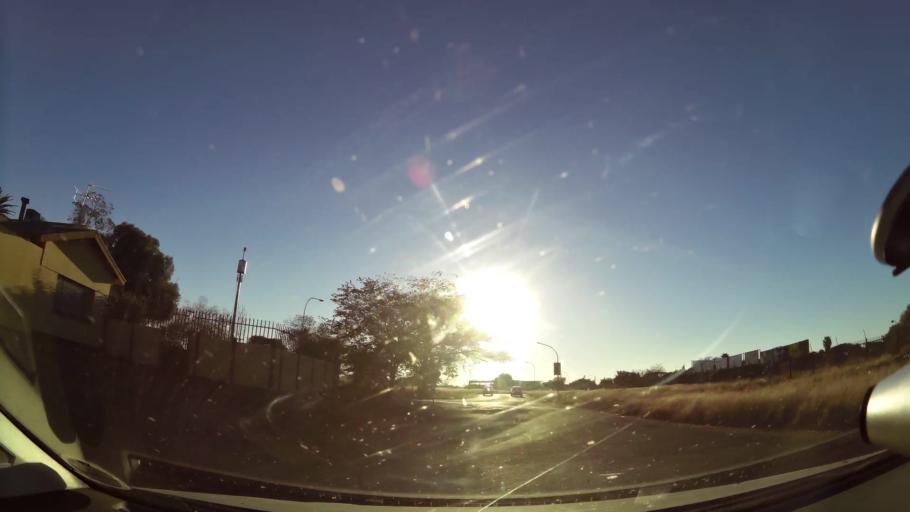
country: ZA
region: Northern Cape
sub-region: Frances Baard District Municipality
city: Kimberley
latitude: -28.7579
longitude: 24.7484
